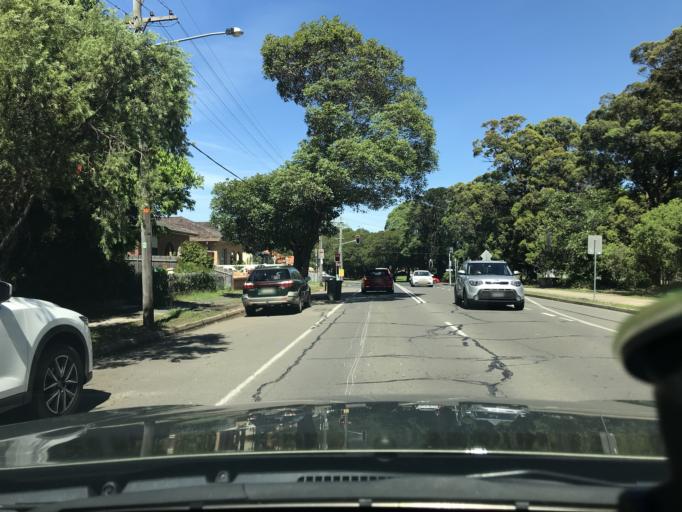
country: AU
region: New South Wales
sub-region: Canada Bay
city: Concord
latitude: -33.8643
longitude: 151.1043
